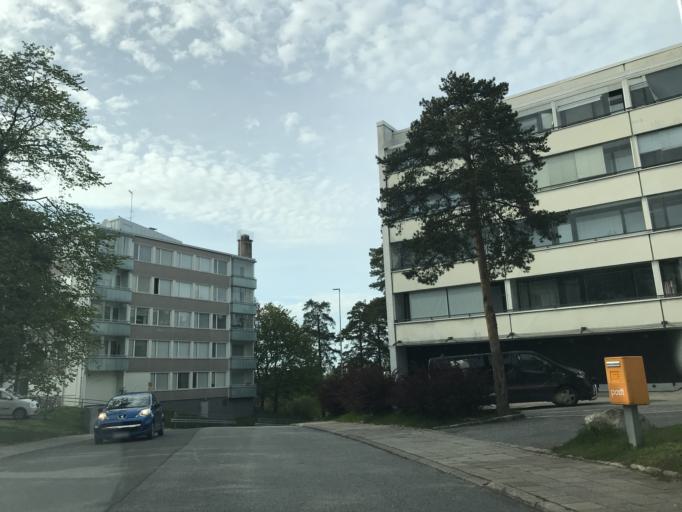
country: FI
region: Varsinais-Suomi
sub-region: Turku
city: Turku
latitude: 60.4347
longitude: 22.3026
